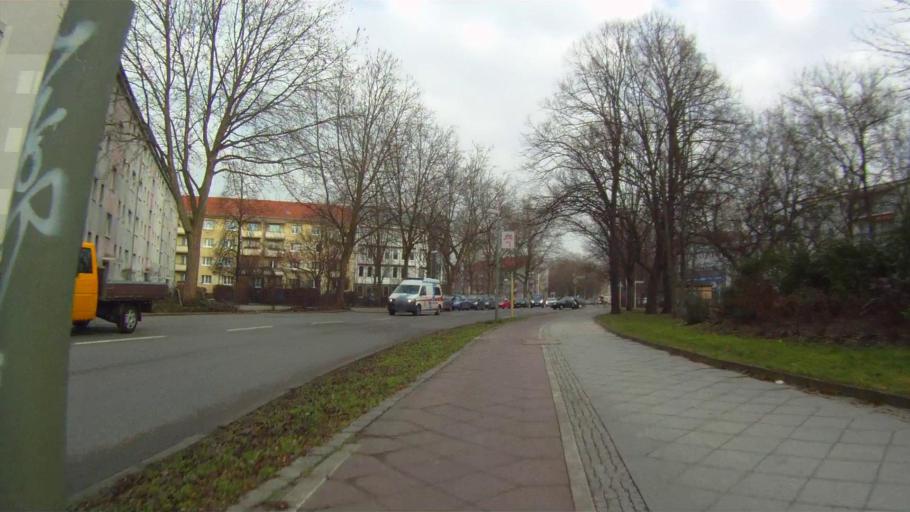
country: DE
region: Berlin
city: Friedrichsfelde
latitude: 52.5035
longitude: 13.5103
